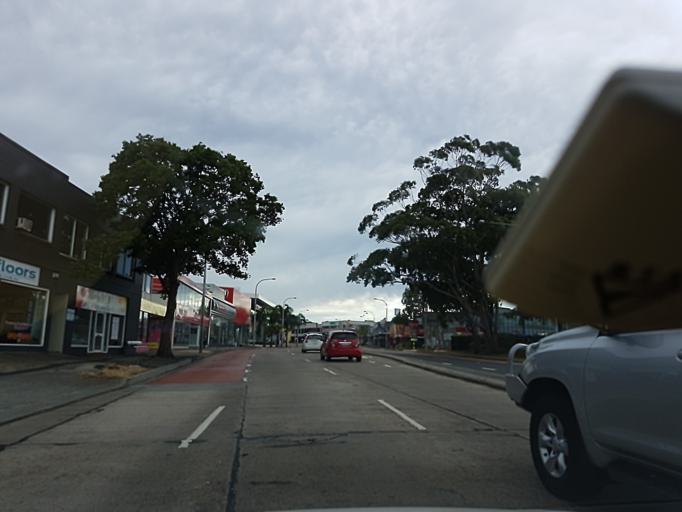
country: AU
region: New South Wales
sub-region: Warringah
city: Brookvale
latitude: -33.7656
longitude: 151.2699
